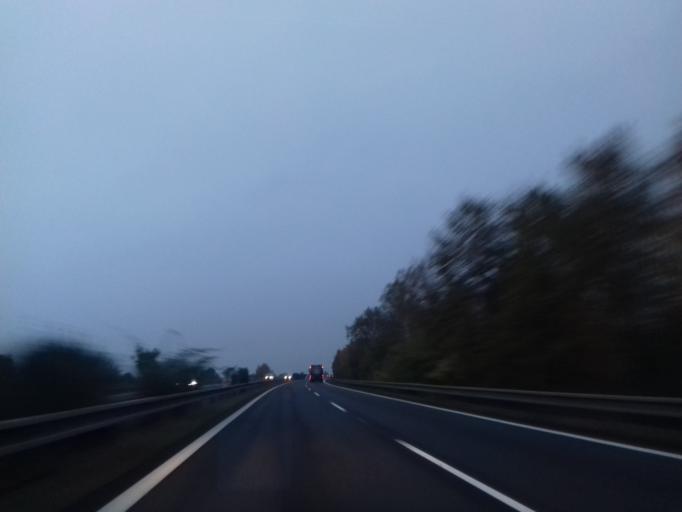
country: CZ
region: Olomoucky
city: Prikazy
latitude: 49.6376
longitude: 17.1447
